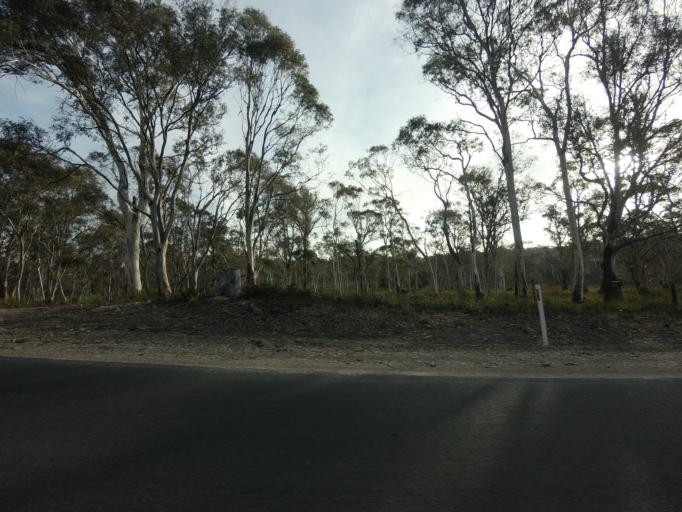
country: AU
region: Tasmania
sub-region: Brighton
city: Bridgewater
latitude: -42.3915
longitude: 147.0446
